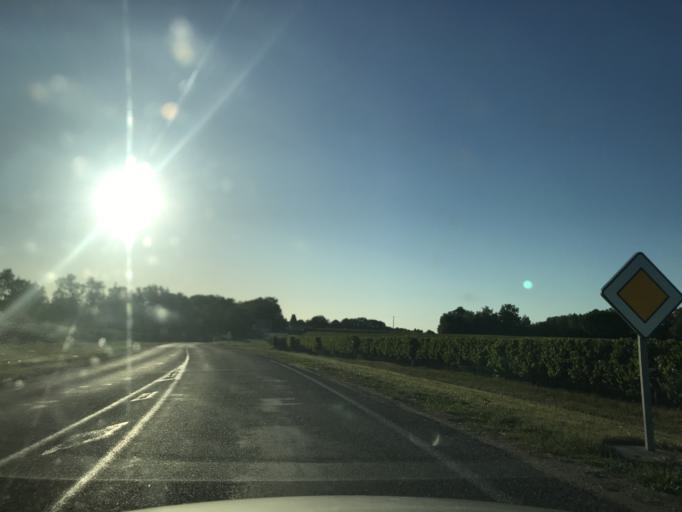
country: FR
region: Aquitaine
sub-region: Departement de la Gironde
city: Mouliets-et-Villemartin
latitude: 44.8936
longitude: -0.0450
